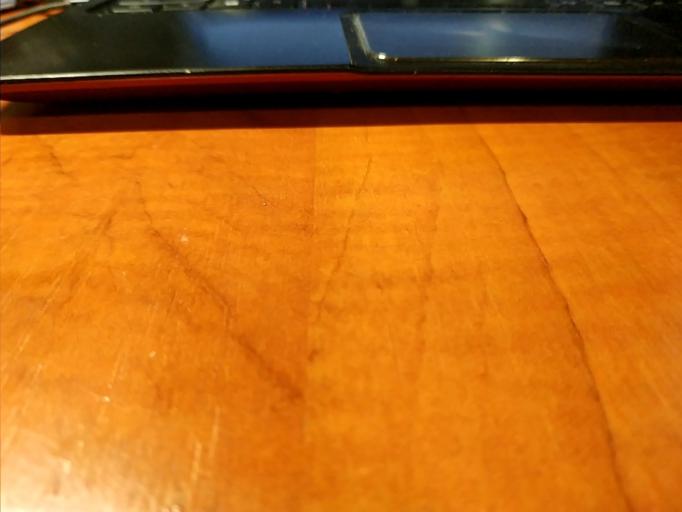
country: RU
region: Tverskaya
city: Ves'yegonsk
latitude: 58.7897
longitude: 37.5438
